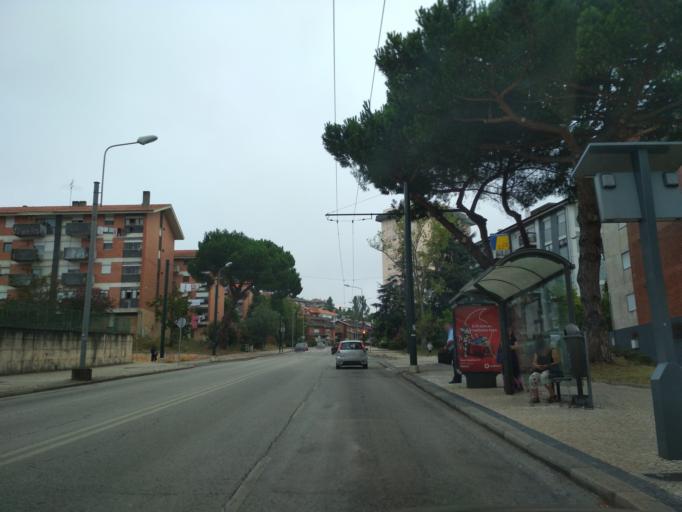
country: PT
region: Coimbra
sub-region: Coimbra
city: Coimbra
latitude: 40.2057
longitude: -8.4041
